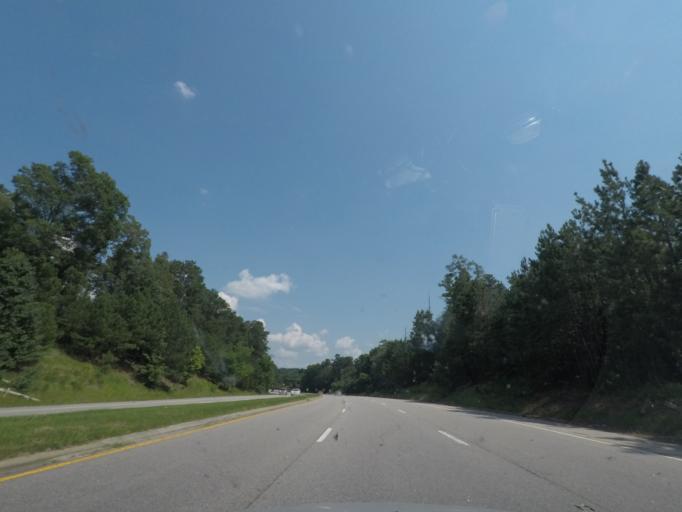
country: US
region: North Carolina
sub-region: Durham County
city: Durham
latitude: 35.9639
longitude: -78.9640
